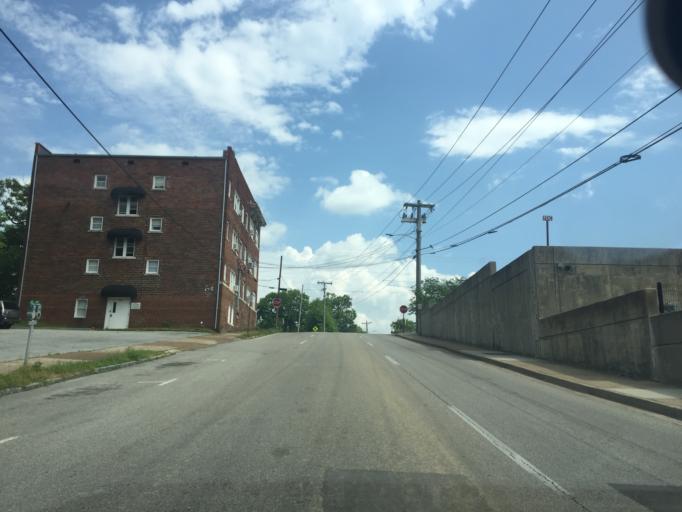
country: US
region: Tennessee
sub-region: Hamilton County
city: Chattanooga
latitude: 35.0456
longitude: -85.3051
